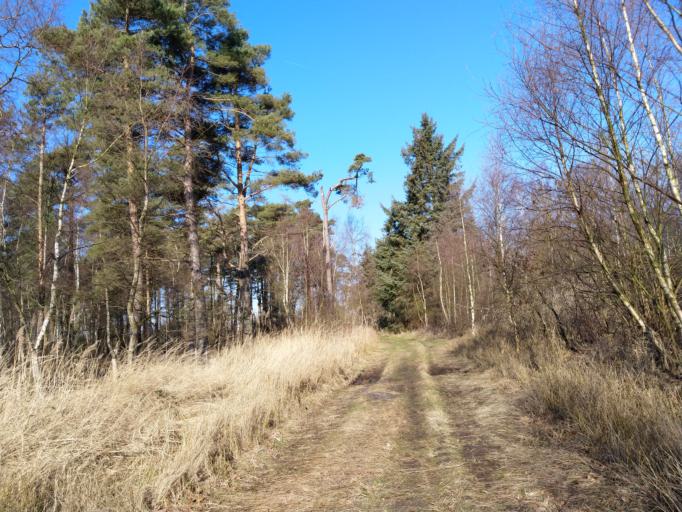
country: DK
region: Zealand
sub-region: Guldborgsund Kommune
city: Nykobing Falster
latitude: 54.6443
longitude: 11.9564
